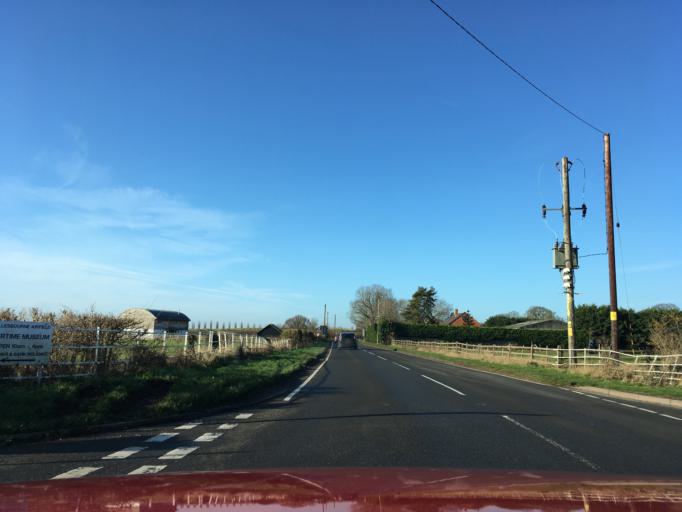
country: GB
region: England
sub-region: Warwickshire
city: Wellesbourne Mountford
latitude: 52.1986
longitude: -1.6177
